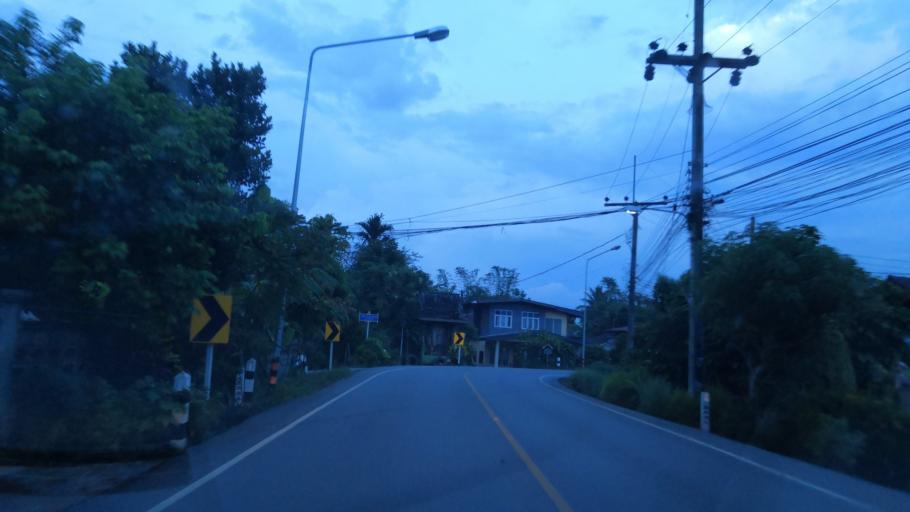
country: TH
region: Chiang Rai
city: Wiang Chai
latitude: 19.9178
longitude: 99.8902
